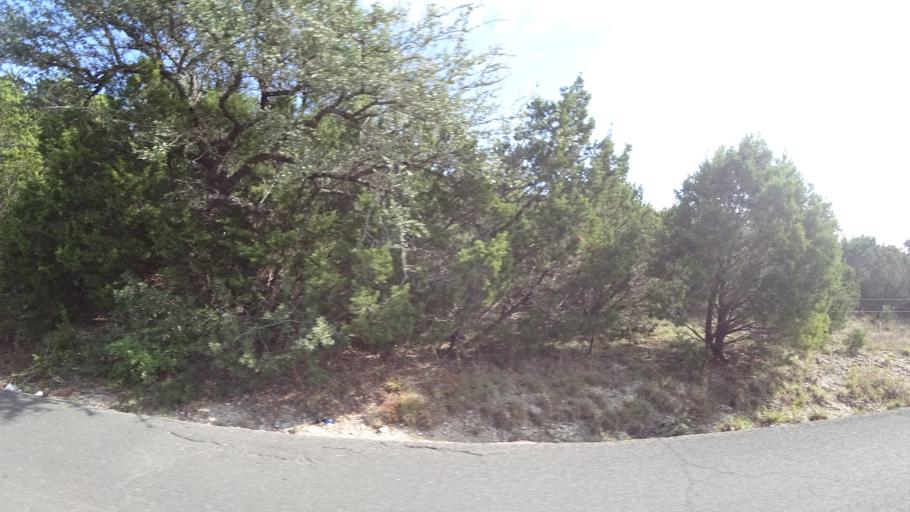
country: US
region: Texas
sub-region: Travis County
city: Barton Creek
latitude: 30.2302
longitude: -97.9270
